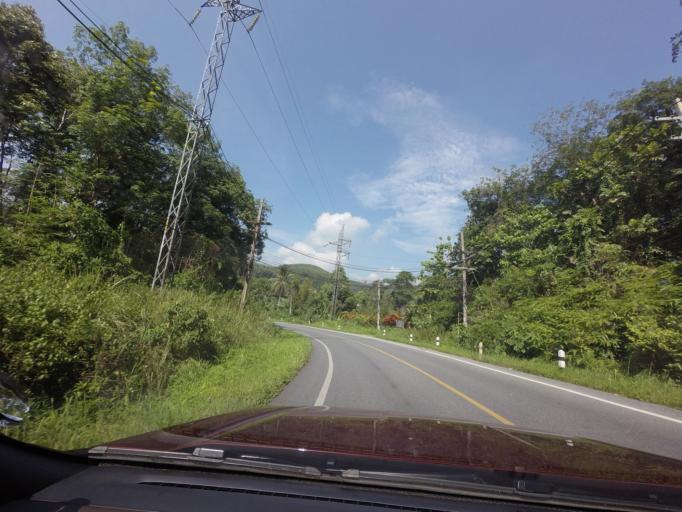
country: TH
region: Yala
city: Betong
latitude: 5.8628
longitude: 101.1259
